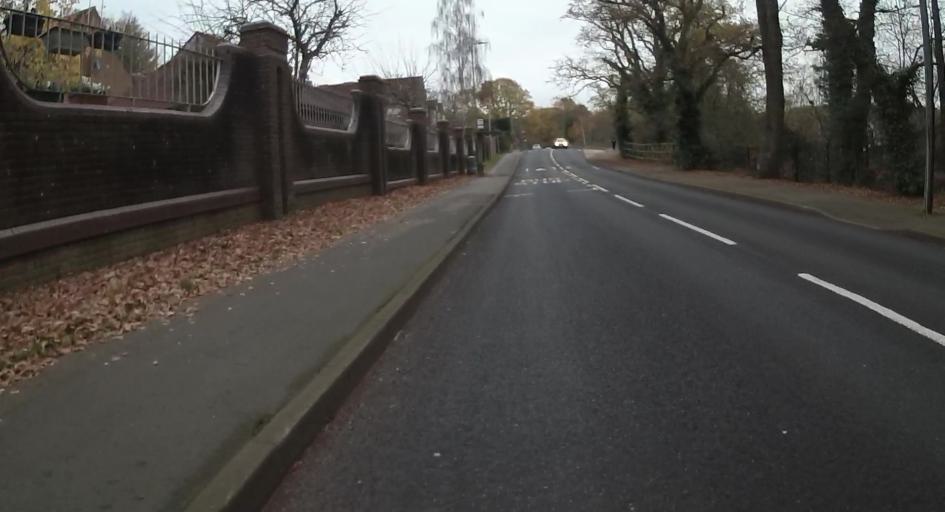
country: GB
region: England
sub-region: Surrey
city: Frimley
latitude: 51.3216
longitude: -0.7259
